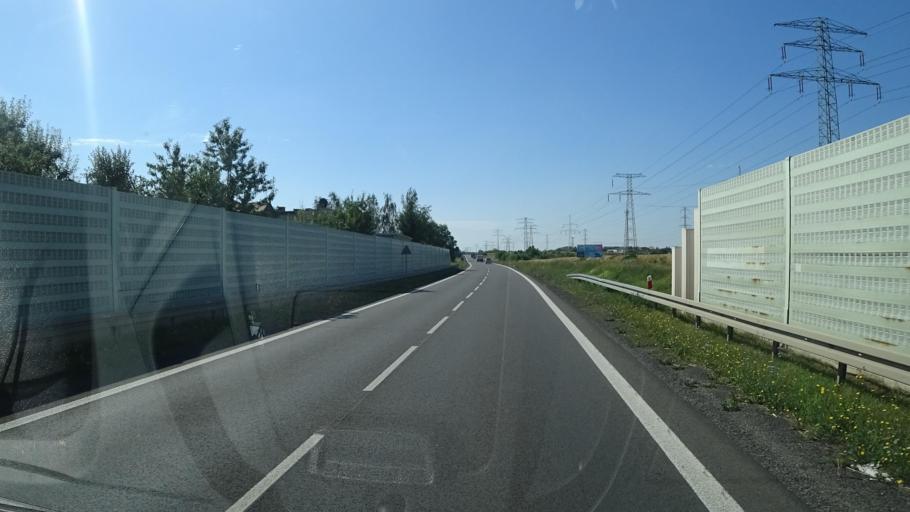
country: PL
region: Greater Poland Voivodeship
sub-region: Powiat koninski
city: Slesin
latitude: 52.3683
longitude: 18.2962
